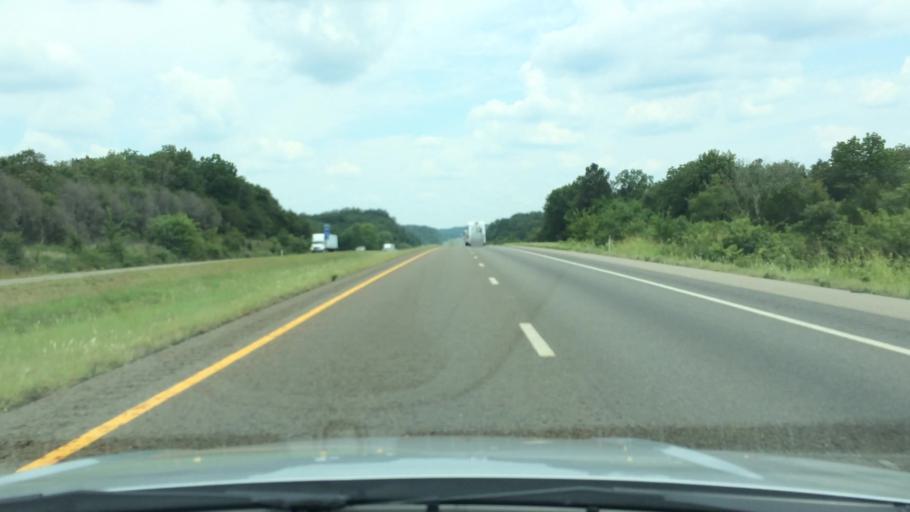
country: US
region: Tennessee
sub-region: Maury County
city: Columbia
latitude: 35.5917
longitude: -86.9023
